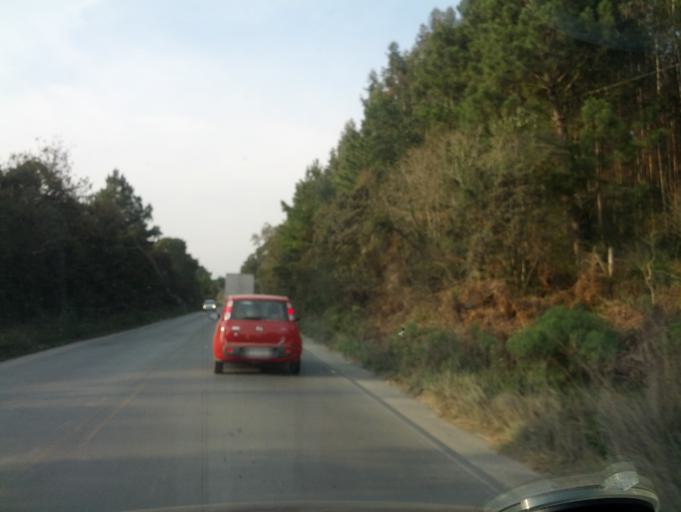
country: BR
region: Santa Catarina
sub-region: Otacilio Costa
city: Otacilio Costa
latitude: -27.5296
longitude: -50.1402
